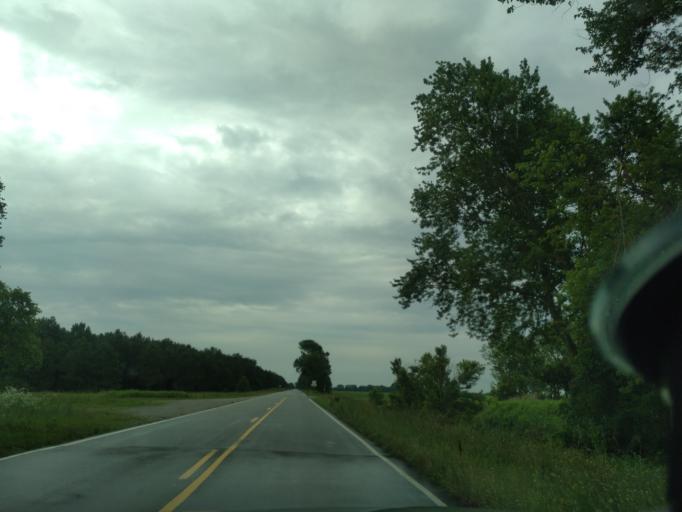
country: US
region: North Carolina
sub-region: Washington County
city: Plymouth
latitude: 35.8498
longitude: -76.5622
